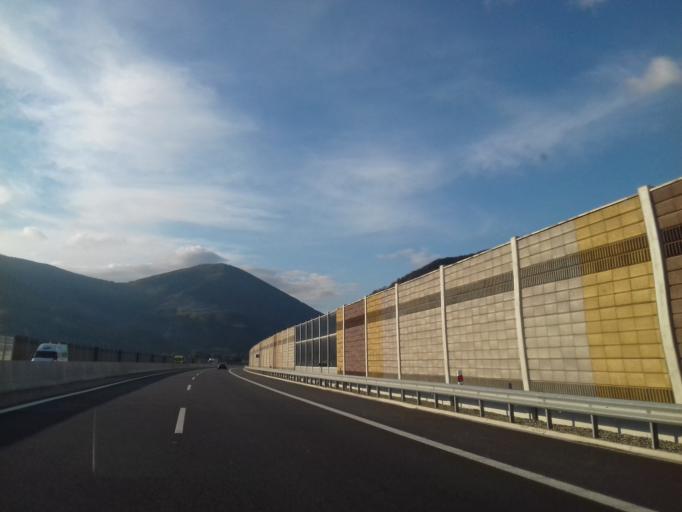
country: SK
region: Zilinsky
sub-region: Okres Zilina
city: Vrutky
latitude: 49.1251
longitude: 18.9176
